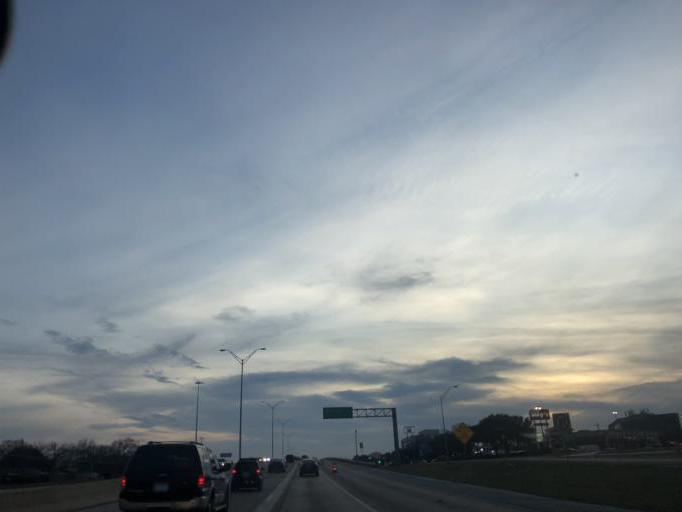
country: US
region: Texas
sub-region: Dallas County
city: Duncanville
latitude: 32.6795
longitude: -96.8545
